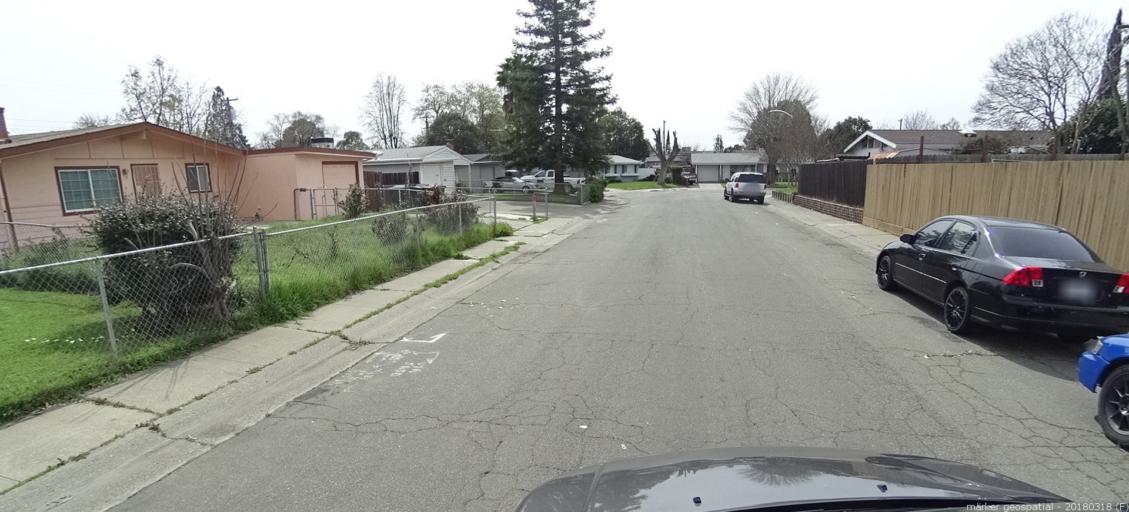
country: US
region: California
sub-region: Sacramento County
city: Parkway
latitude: 38.5185
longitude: -121.4570
